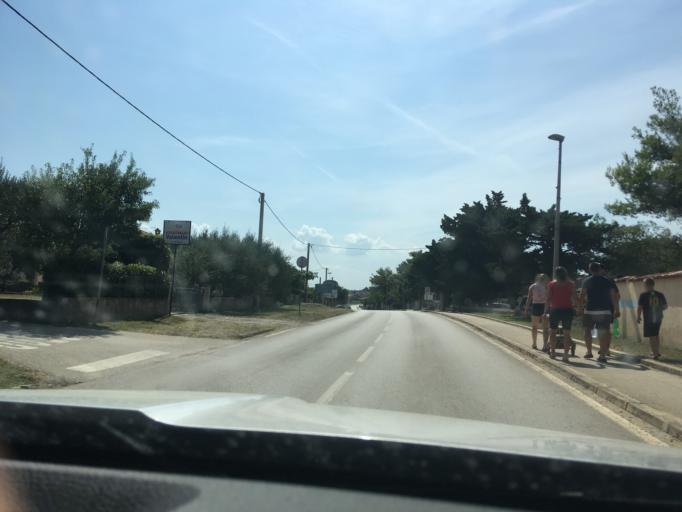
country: HR
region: Zadarska
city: Privlaka
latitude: 44.2573
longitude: 15.1251
